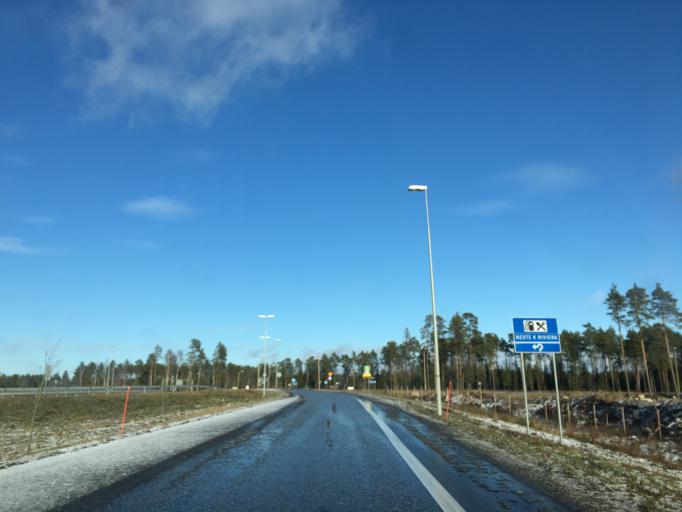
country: FI
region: Varsinais-Suomi
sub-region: Turku
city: Masku
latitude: 60.5412
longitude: 22.1277
